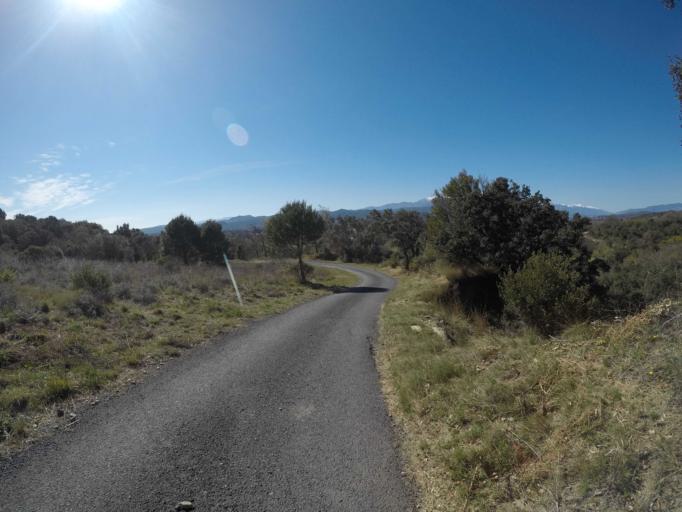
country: FR
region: Languedoc-Roussillon
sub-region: Departement des Pyrenees-Orientales
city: Millas
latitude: 42.7037
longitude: 2.6676
